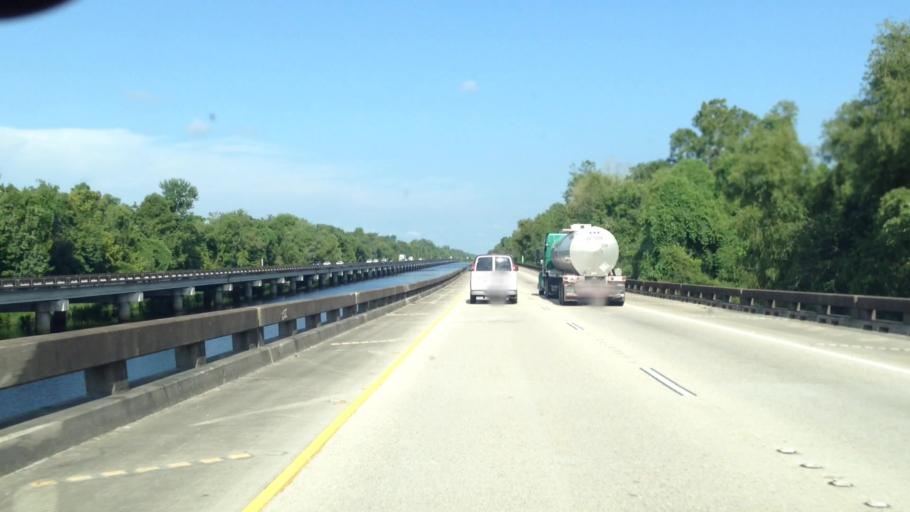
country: US
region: Louisiana
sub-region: Saint John the Baptist Parish
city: Reserve
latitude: 30.1117
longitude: -90.5490
